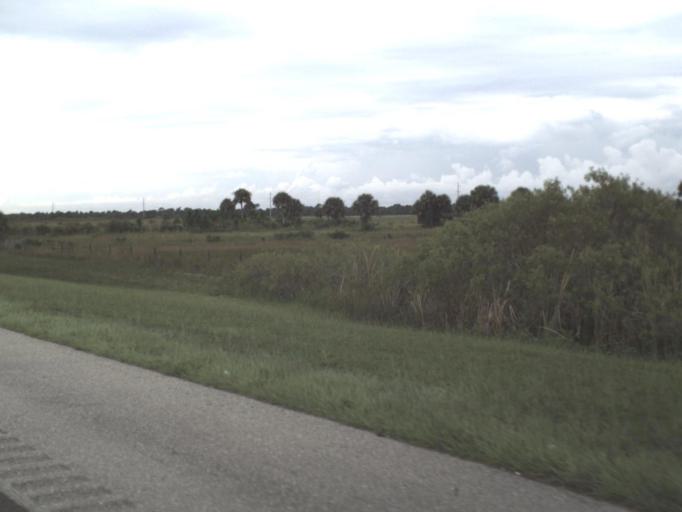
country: US
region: Florida
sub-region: Sarasota County
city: Osprey
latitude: 27.2066
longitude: -82.4431
